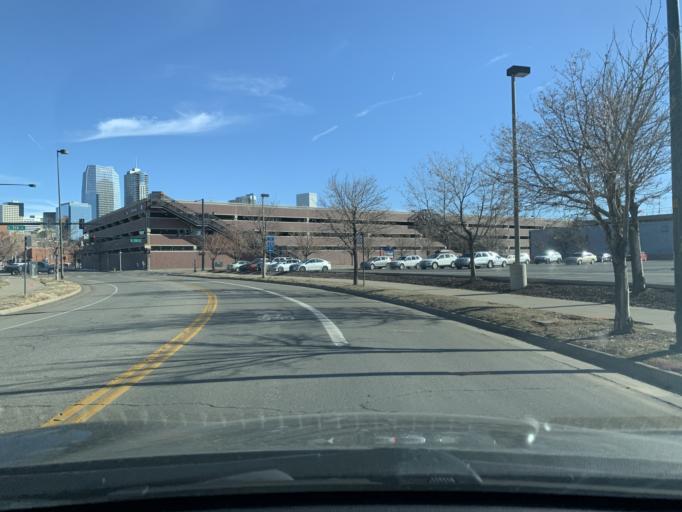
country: US
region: Colorado
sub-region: Denver County
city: Denver
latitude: 39.7436
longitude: -105.0096
